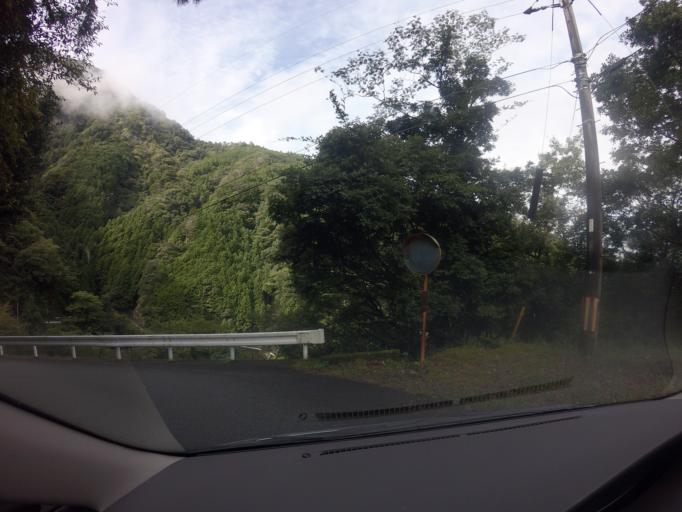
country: JP
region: Wakayama
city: Shingu
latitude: 33.9686
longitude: 135.8105
